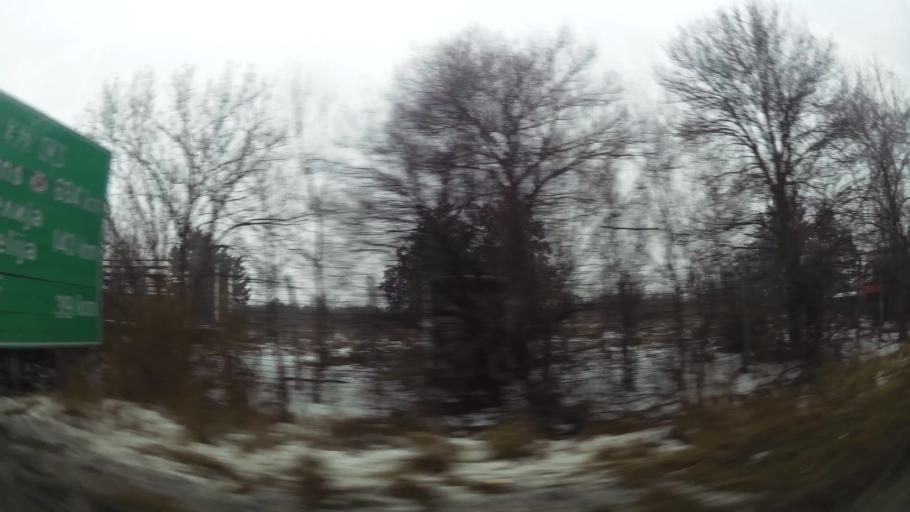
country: MK
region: Petrovec
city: Petrovec
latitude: 41.9502
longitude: 21.6308
